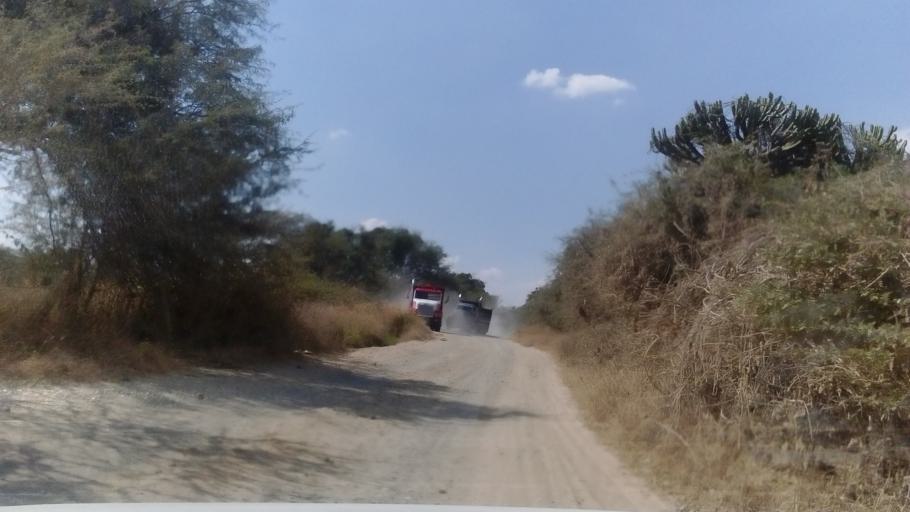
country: MX
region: Guanajuato
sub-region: Silao de la Victoria
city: San Francisco (Banos de Agua Caliente)
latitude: 21.0723
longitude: -101.4660
